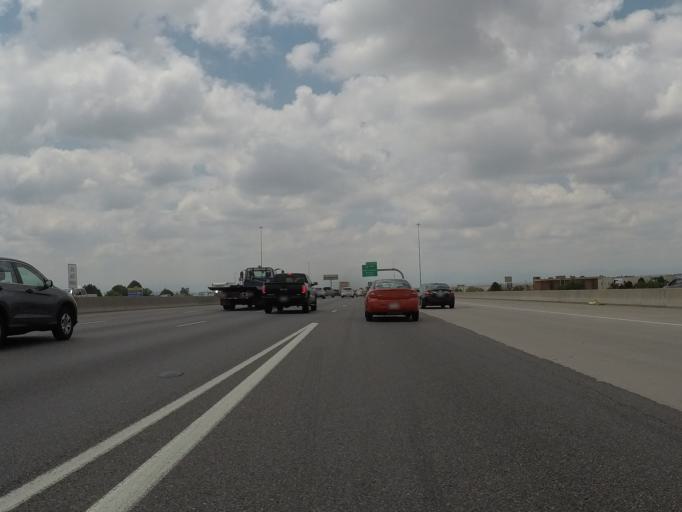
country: US
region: Colorado
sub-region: Adams County
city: Aurora
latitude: 39.7738
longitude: -104.8417
